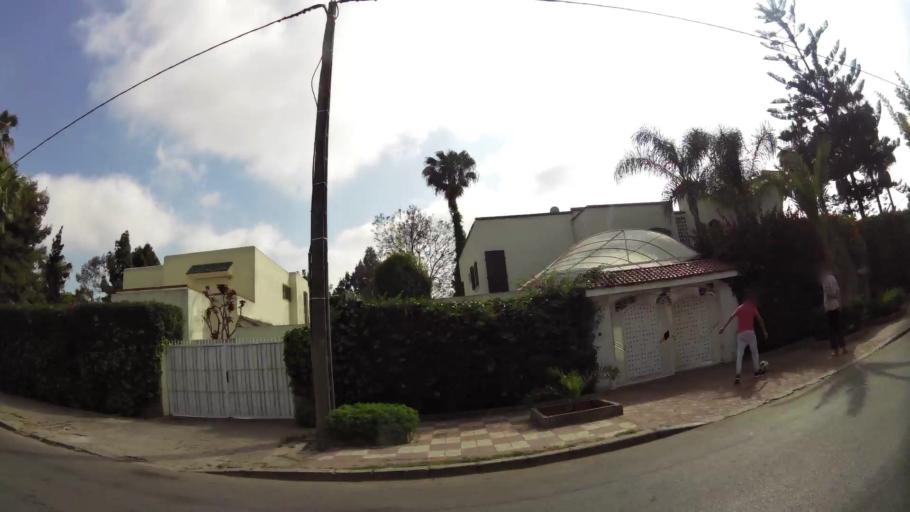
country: MA
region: Rabat-Sale-Zemmour-Zaer
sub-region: Rabat
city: Rabat
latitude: 33.9710
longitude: -6.8581
